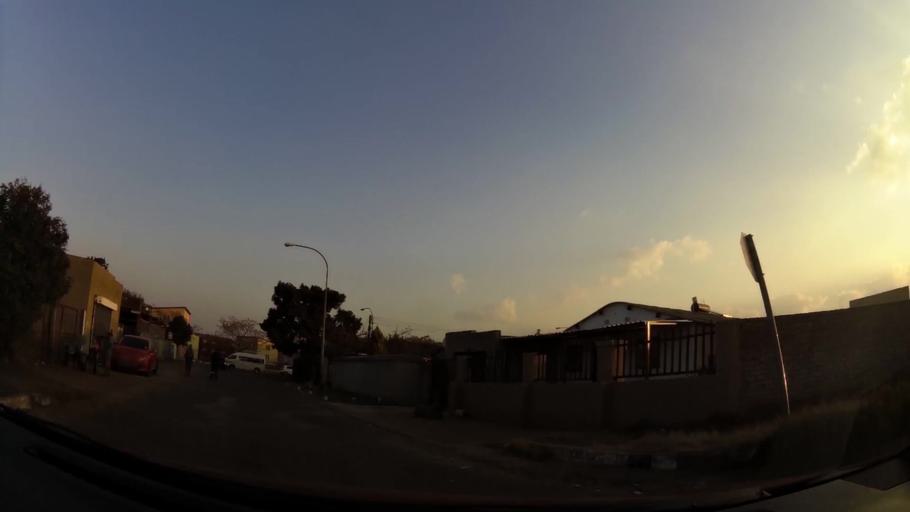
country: ZA
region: Gauteng
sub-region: City of Johannesburg Metropolitan Municipality
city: Soweto
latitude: -26.2912
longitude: 27.8977
